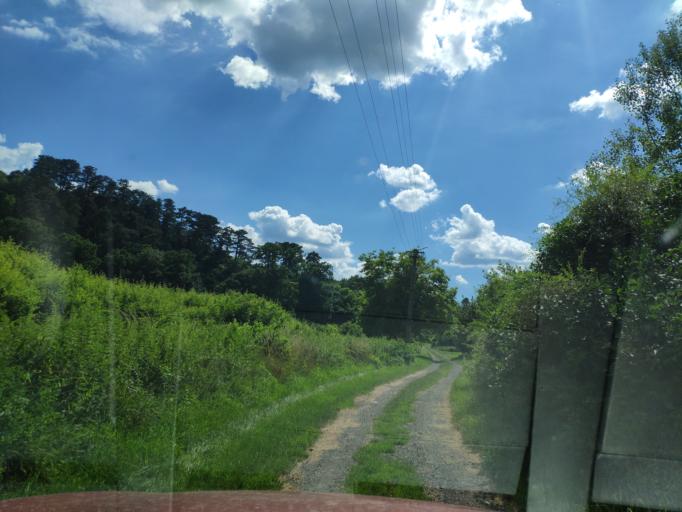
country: HU
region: Borsod-Abauj-Zemplen
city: Arlo
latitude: 48.2781
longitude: 20.1889
